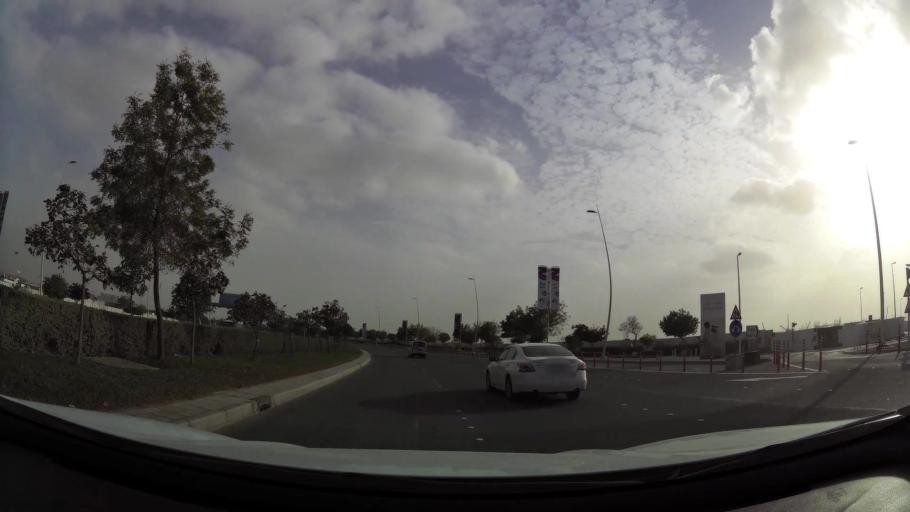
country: AE
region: Abu Dhabi
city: Abu Dhabi
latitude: 24.4937
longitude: 54.5907
